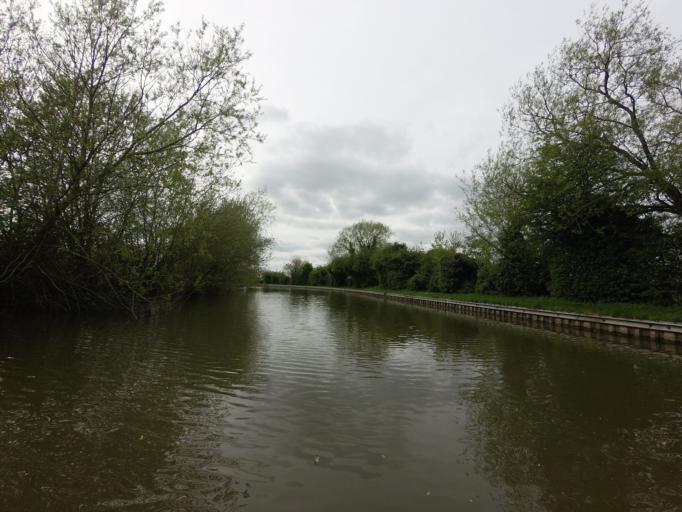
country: GB
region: England
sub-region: Milton Keynes
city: Bradwell
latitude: 52.0742
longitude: -0.7805
